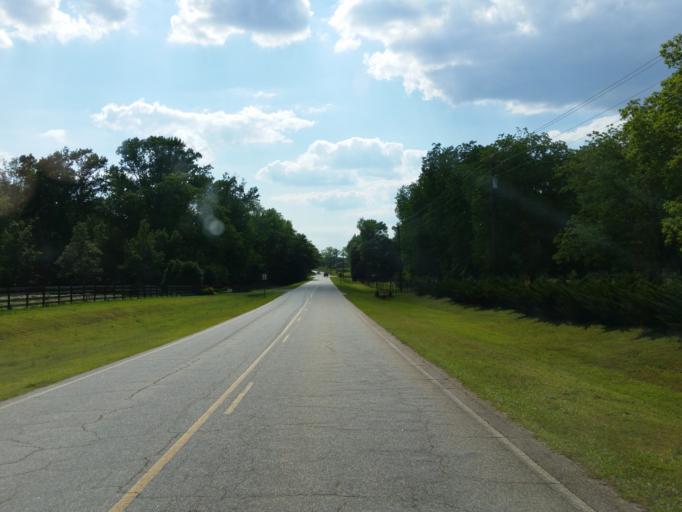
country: US
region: Georgia
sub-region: Houston County
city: Centerville
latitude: 32.5782
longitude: -83.7458
